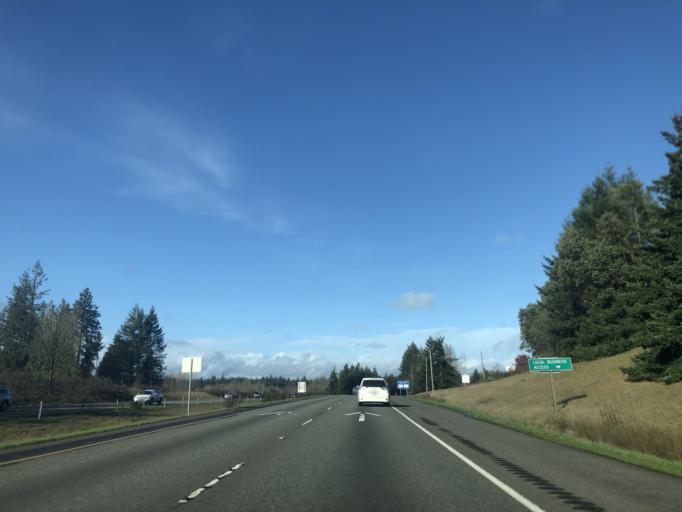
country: US
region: Washington
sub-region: Pierce County
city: Gig Harbor
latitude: 47.3355
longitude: -122.6035
